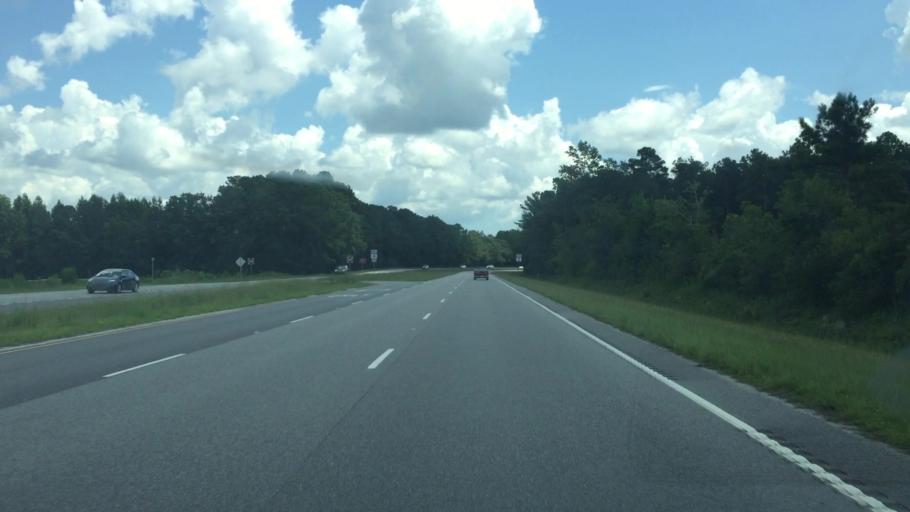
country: US
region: South Carolina
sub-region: Horry County
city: Loris
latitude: 34.0337
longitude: -78.8080
